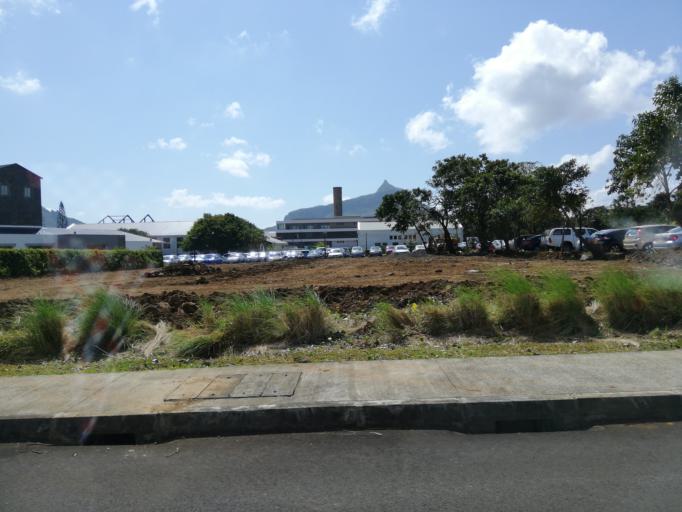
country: MU
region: Moka
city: Verdun
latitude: -20.2264
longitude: 57.5354
